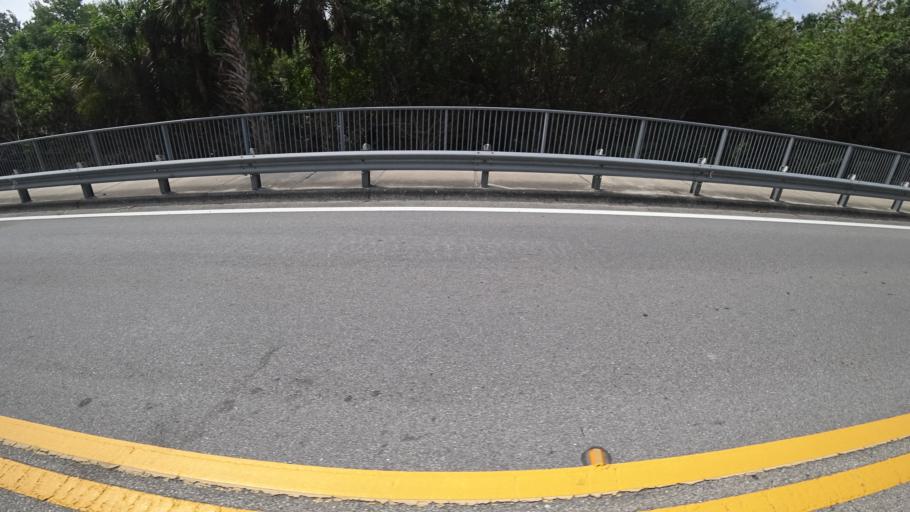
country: US
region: Florida
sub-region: Sarasota County
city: North Sarasota
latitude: 27.4180
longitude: -82.5092
